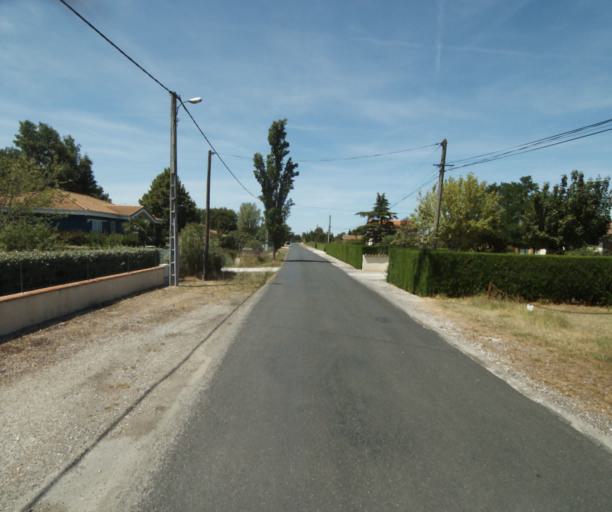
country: FR
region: Midi-Pyrenees
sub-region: Departement de la Haute-Garonne
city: Revel
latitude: 43.4853
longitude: 2.0232
